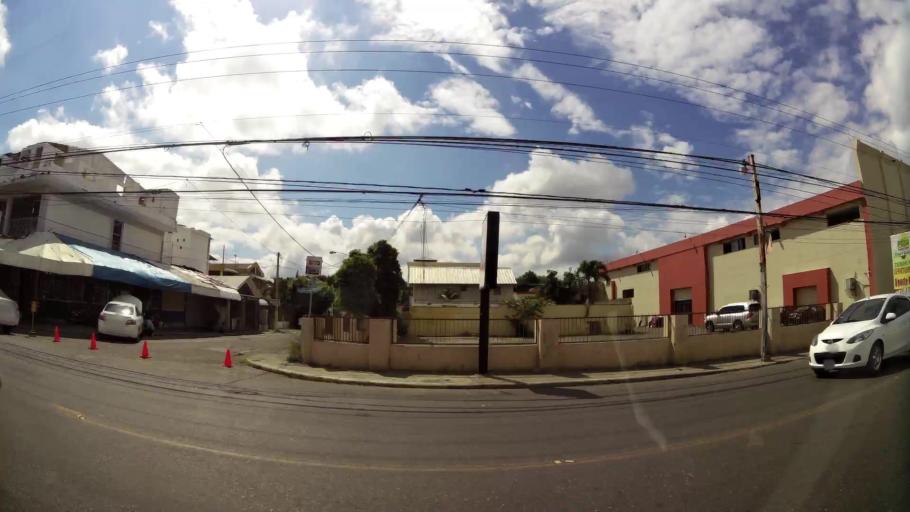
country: DO
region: Santiago
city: Santiago de los Caballeros
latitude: 19.4655
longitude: -70.6924
